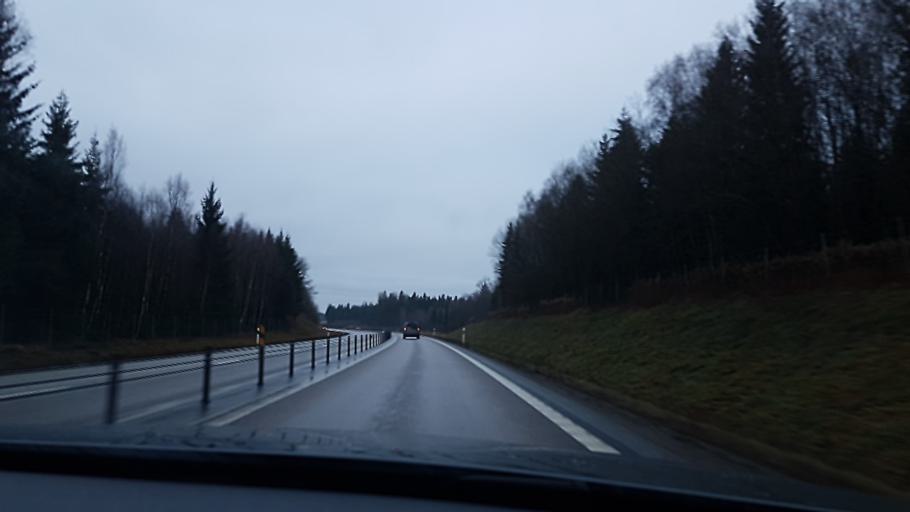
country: SE
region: Kronoberg
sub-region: Ljungby Kommun
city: Lagan
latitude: 56.9842
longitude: 14.0189
